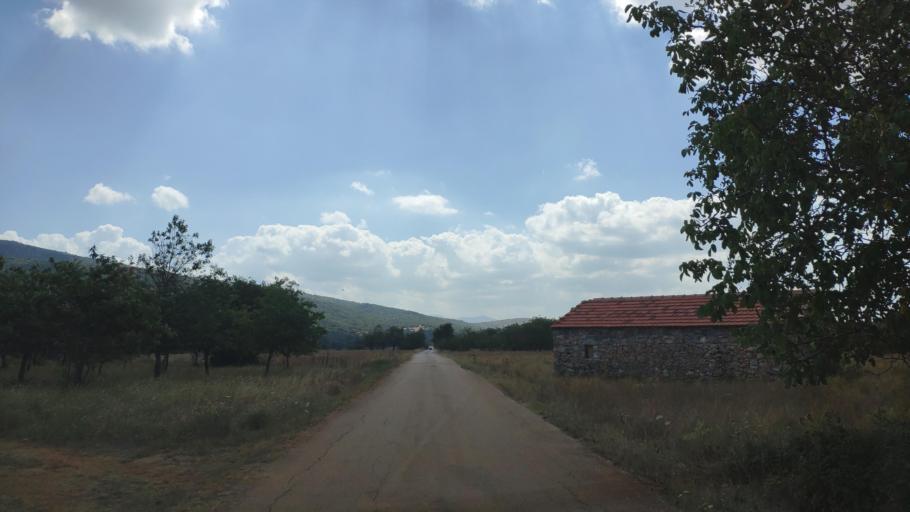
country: GR
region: Peloponnese
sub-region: Nomos Lakonias
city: Kariai
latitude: 37.3163
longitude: 22.4413
